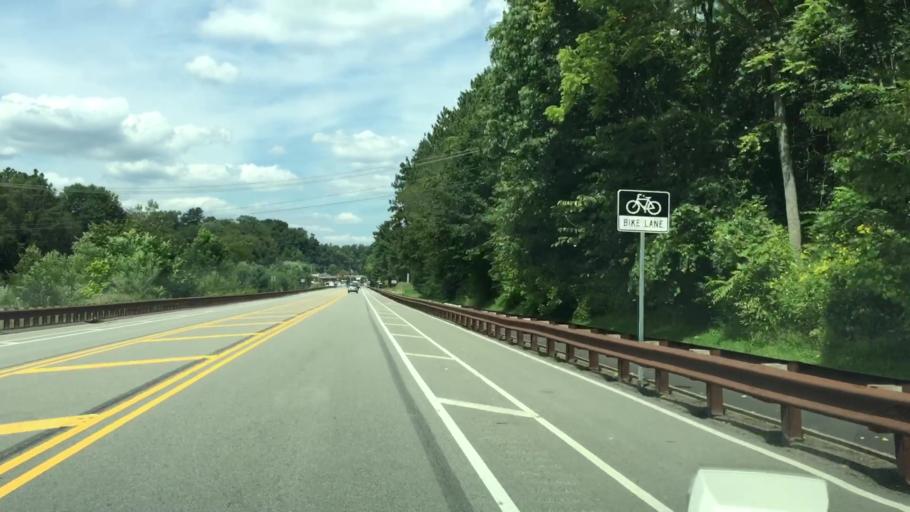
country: US
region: Pennsylvania
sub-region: Allegheny County
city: Bethel Park
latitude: 40.3266
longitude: -80.0180
